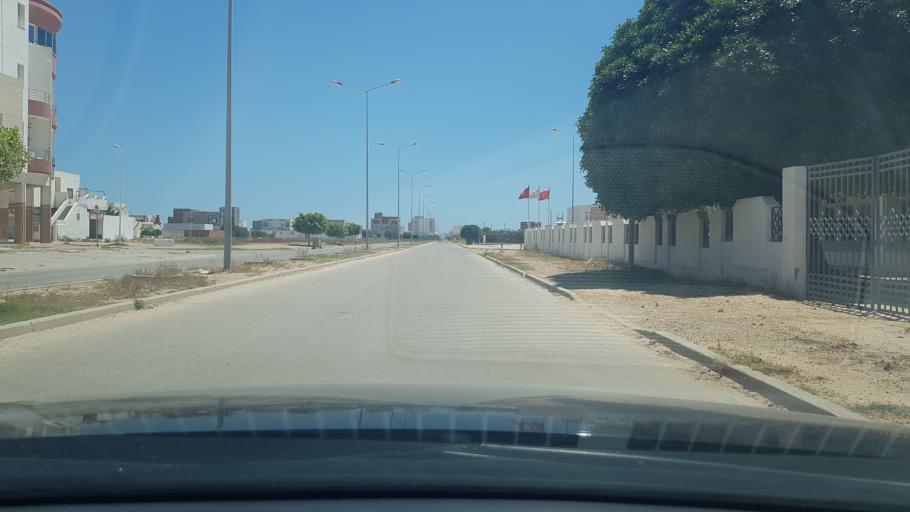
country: TN
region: Safaqis
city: Al Qarmadah
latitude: 34.8409
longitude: 10.7568
